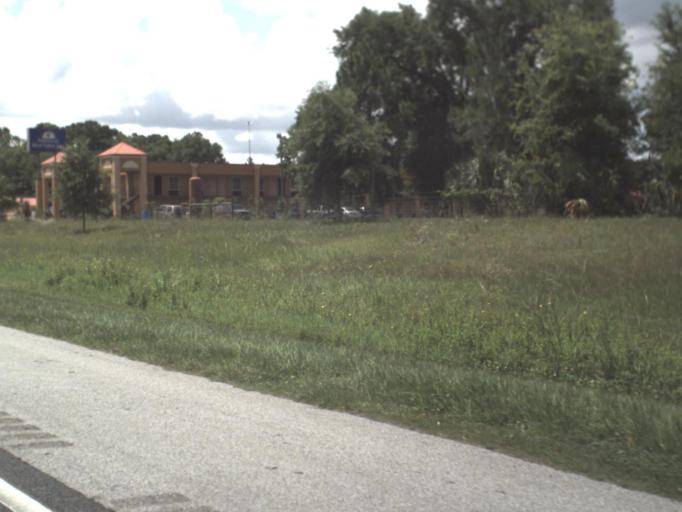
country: US
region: Florida
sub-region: Suwannee County
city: Wellborn
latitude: 30.3184
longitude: -82.8086
